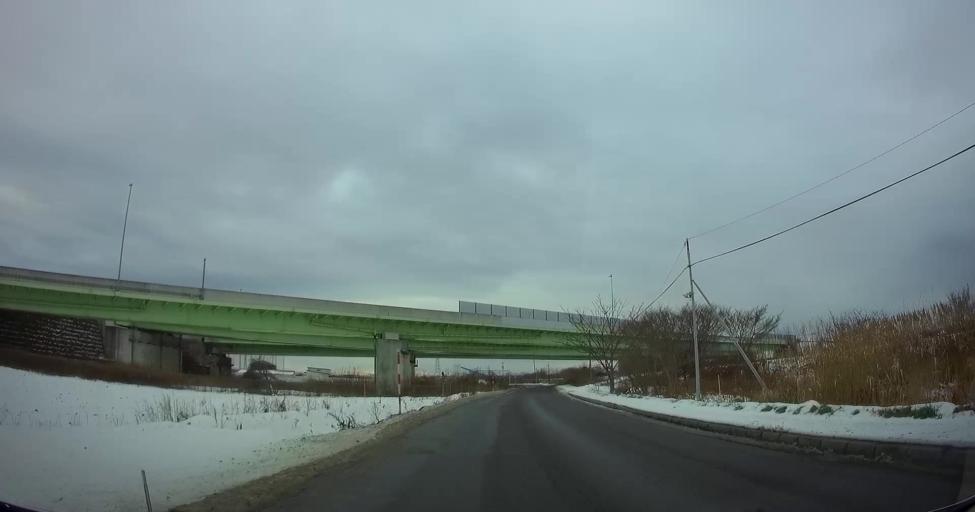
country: JP
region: Hokkaido
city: Kamiiso
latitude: 41.8349
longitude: 140.6909
